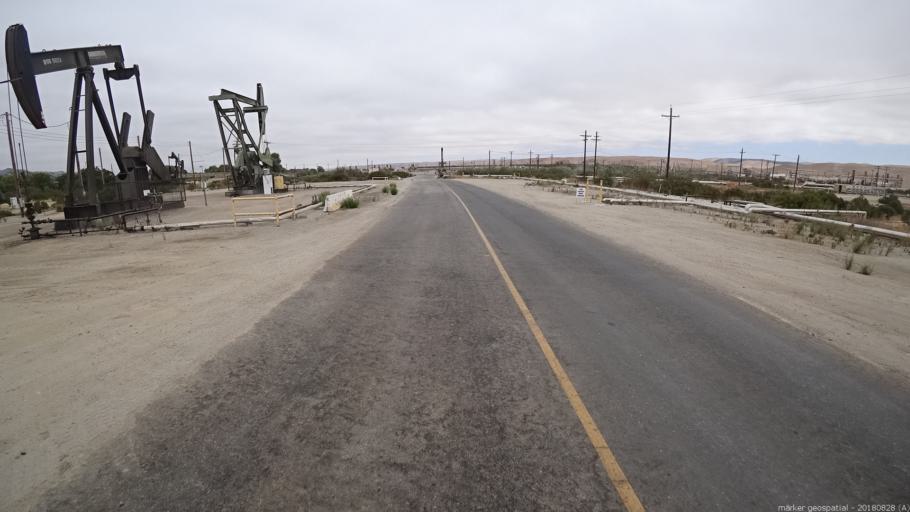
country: US
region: California
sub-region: San Luis Obispo County
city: Lake Nacimiento
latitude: 35.9605
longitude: -120.8793
